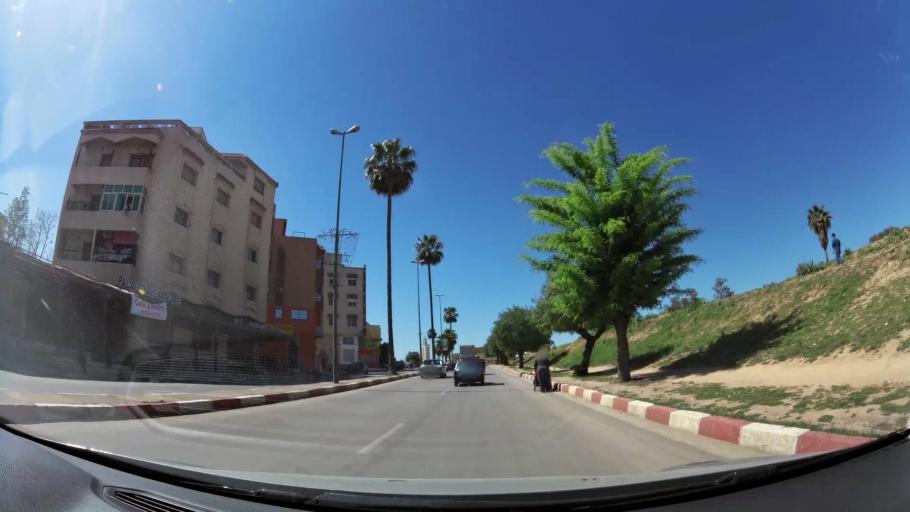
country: MA
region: Meknes-Tafilalet
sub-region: Meknes
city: Meknes
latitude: 33.8758
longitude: -5.5594
